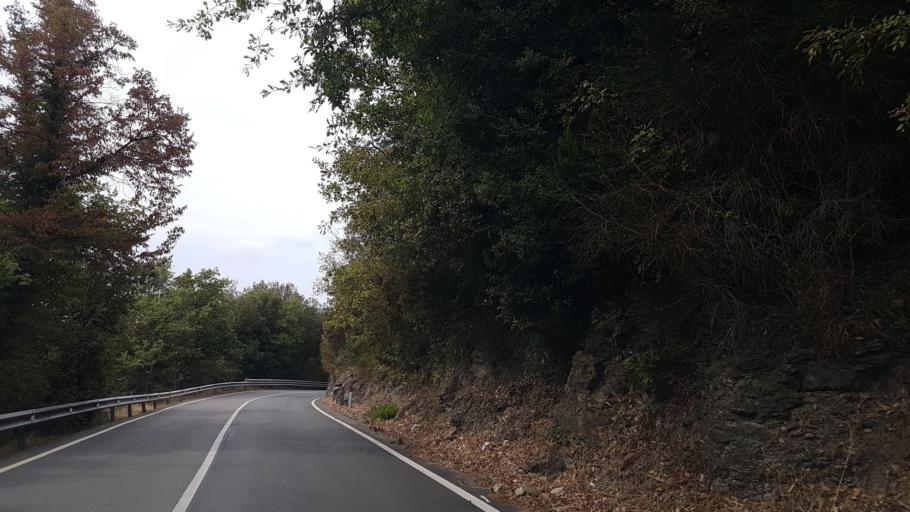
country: IT
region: Liguria
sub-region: Provincia di Genova
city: Moneglia
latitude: 44.2579
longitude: 9.4978
